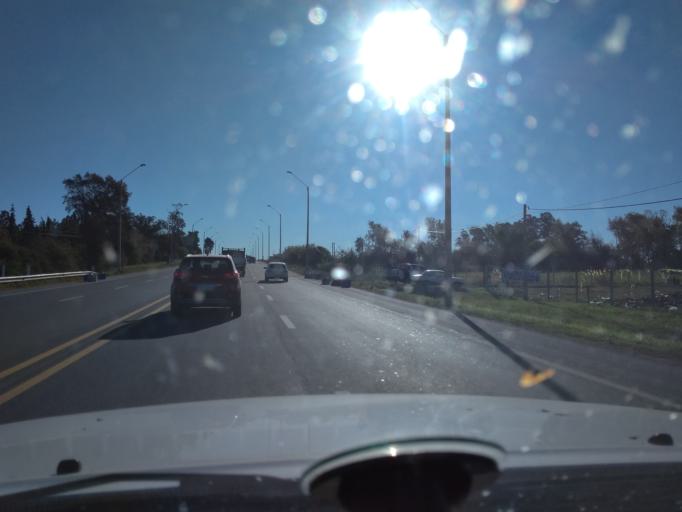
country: UY
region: Canelones
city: Colonia Nicolich
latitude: -34.8025
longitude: -56.0543
